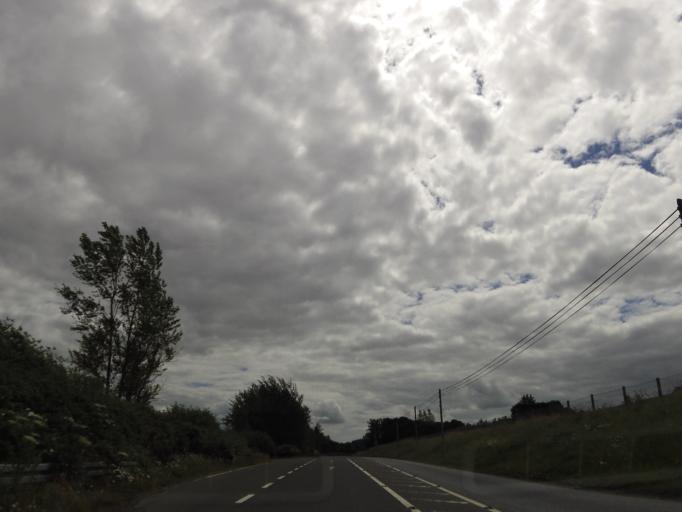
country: IE
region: Munster
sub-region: North Tipperary
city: Templemore
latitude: 52.7688
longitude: -8.0239
